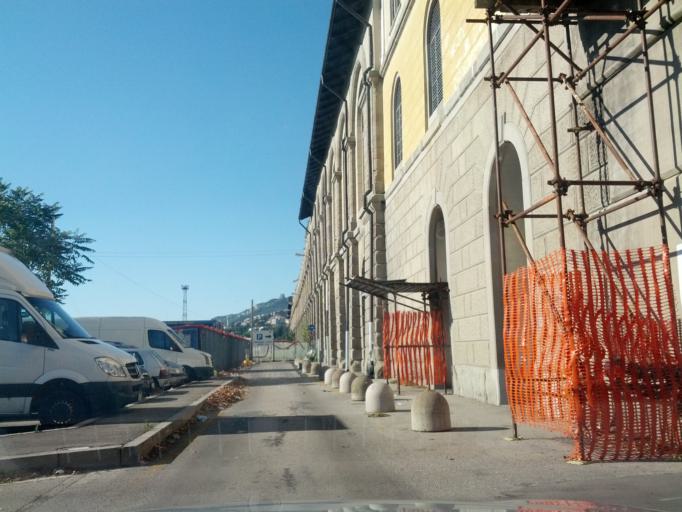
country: IT
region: Friuli Venezia Giulia
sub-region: Provincia di Trieste
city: Trieste
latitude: 45.6571
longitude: 13.7703
